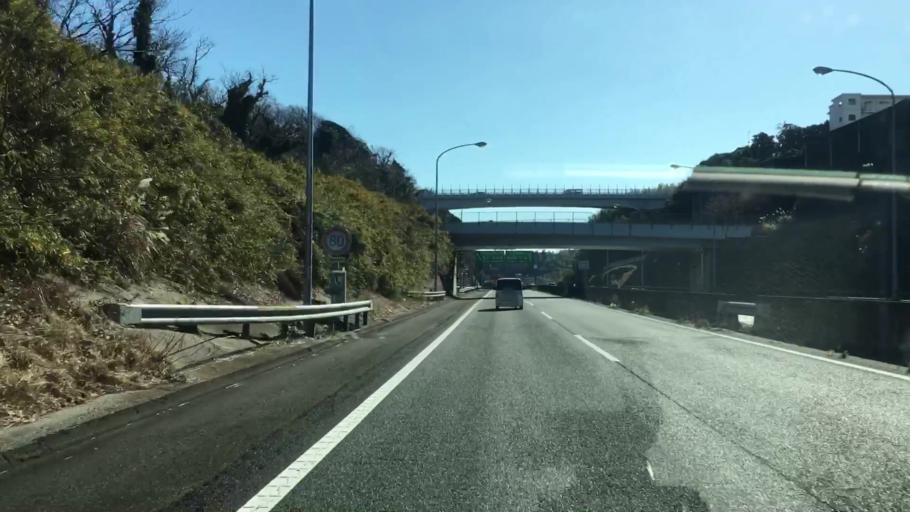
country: JP
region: Kanagawa
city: Kamakura
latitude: 35.3691
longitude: 139.5950
